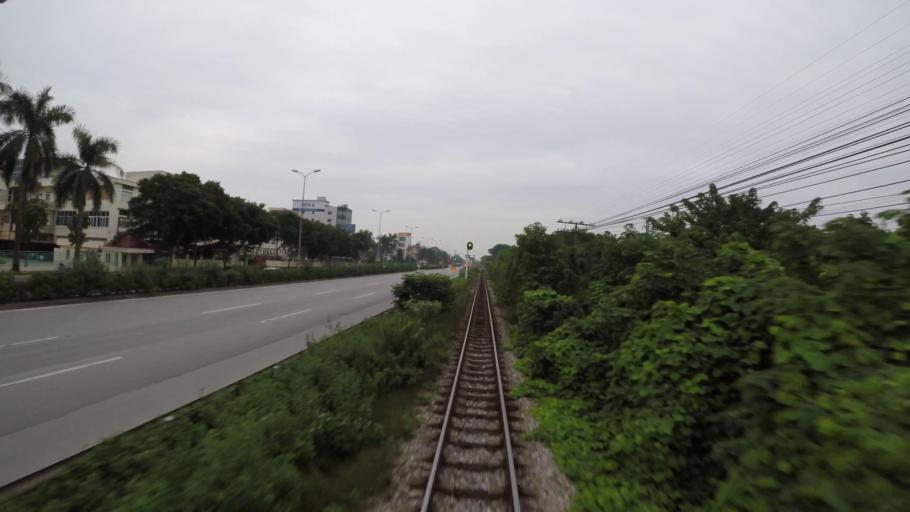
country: VN
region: Ha Noi
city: Trau Quy
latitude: 21.0048
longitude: 105.9605
